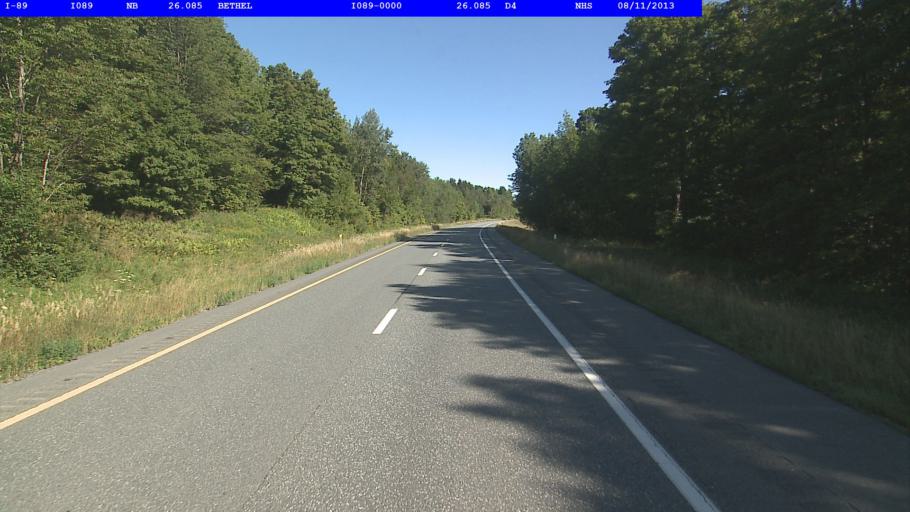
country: US
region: Vermont
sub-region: Orange County
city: Randolph
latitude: 43.8763
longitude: -72.6138
